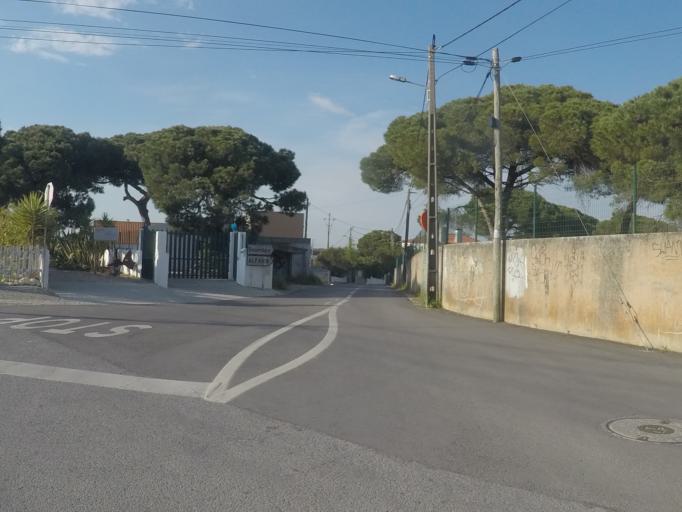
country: PT
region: Setubal
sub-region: Sesimbra
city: Sesimbra
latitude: 38.4698
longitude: -9.1700
